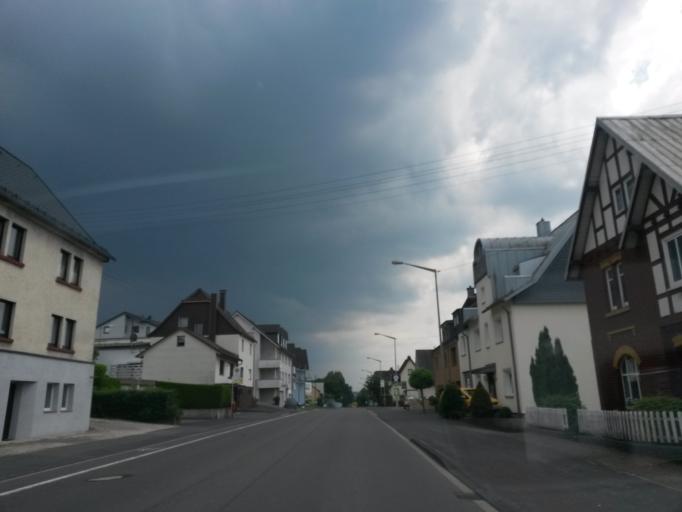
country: DE
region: North Rhine-Westphalia
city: Kreuztal
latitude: 50.9669
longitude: 7.9844
